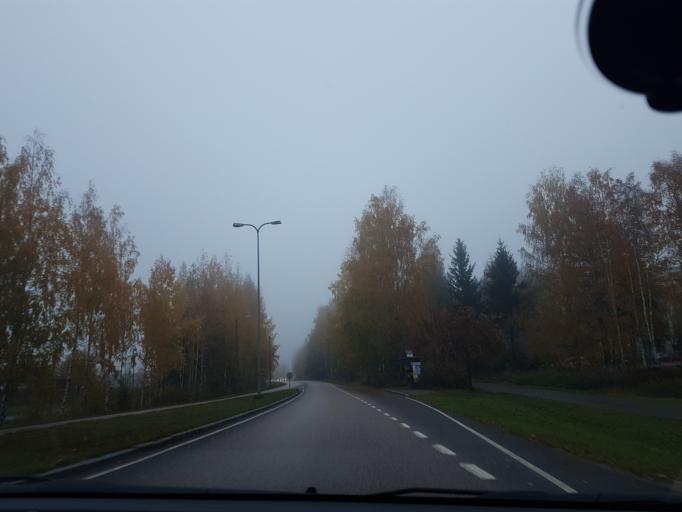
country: FI
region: Uusimaa
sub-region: Helsinki
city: Tuusula
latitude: 60.4041
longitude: 25.0345
